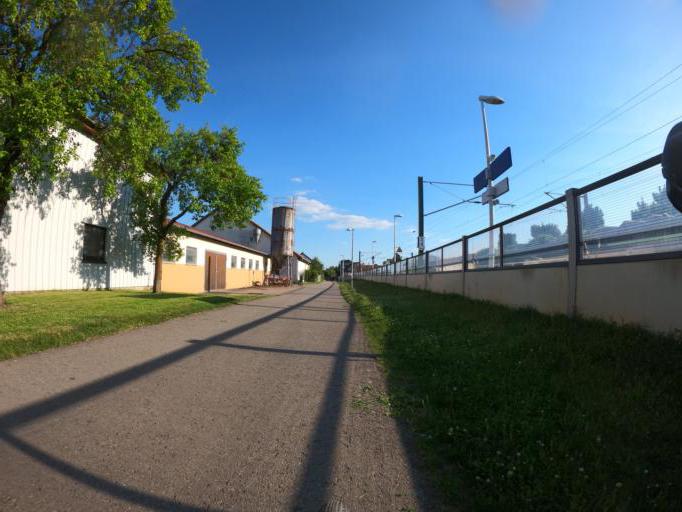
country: DE
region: Baden-Wuerttemberg
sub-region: Regierungsbezirk Stuttgart
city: Magstadt
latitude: 48.7218
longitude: 8.9697
